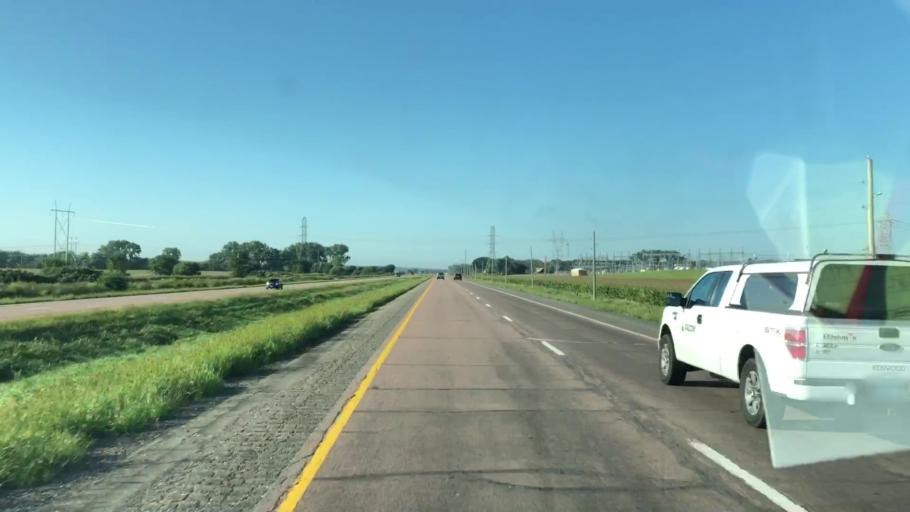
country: US
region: Iowa
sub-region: Woodbury County
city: Sioux City
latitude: 42.6060
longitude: -96.2994
